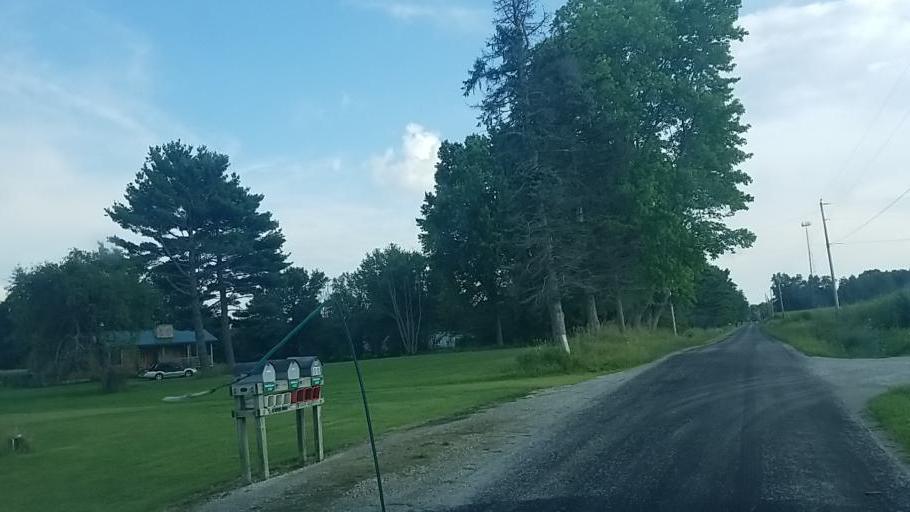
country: US
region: Ohio
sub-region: Wayne County
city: West Salem
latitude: 40.8833
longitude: -82.1925
